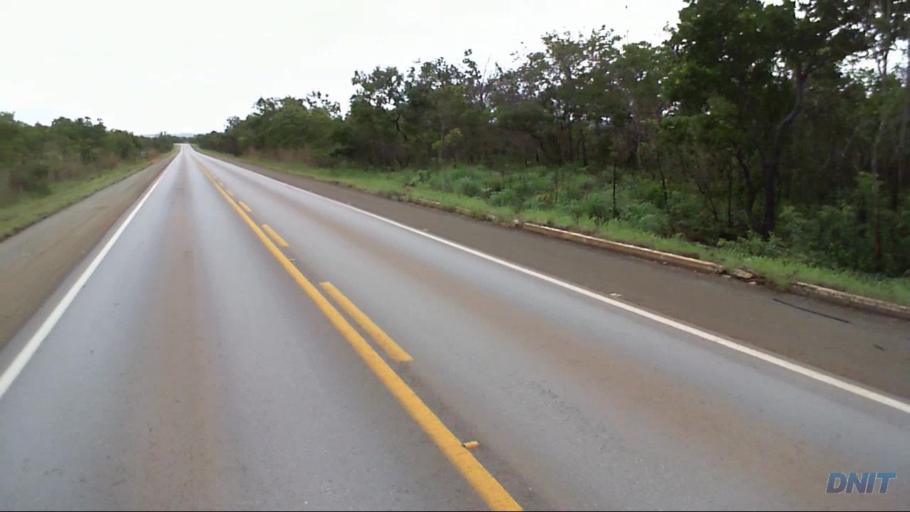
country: BR
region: Goias
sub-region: Barro Alto
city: Barro Alto
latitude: -14.7746
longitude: -49.0574
